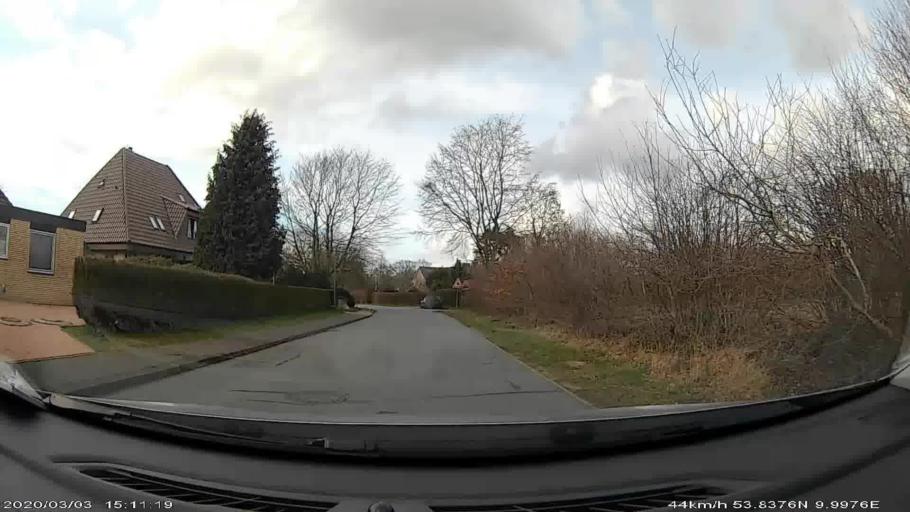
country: DE
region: Schleswig-Holstein
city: Oersdorf
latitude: 53.8373
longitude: 9.9977
